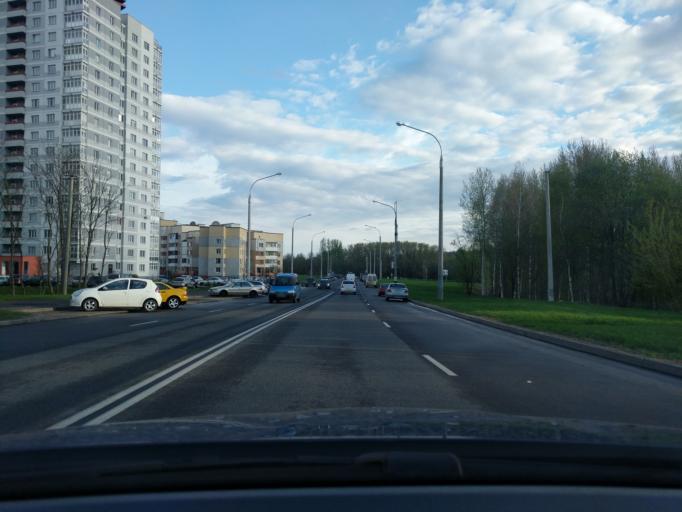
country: BY
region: Minsk
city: Novoye Medvezhino
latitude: 53.8964
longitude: 27.4749
